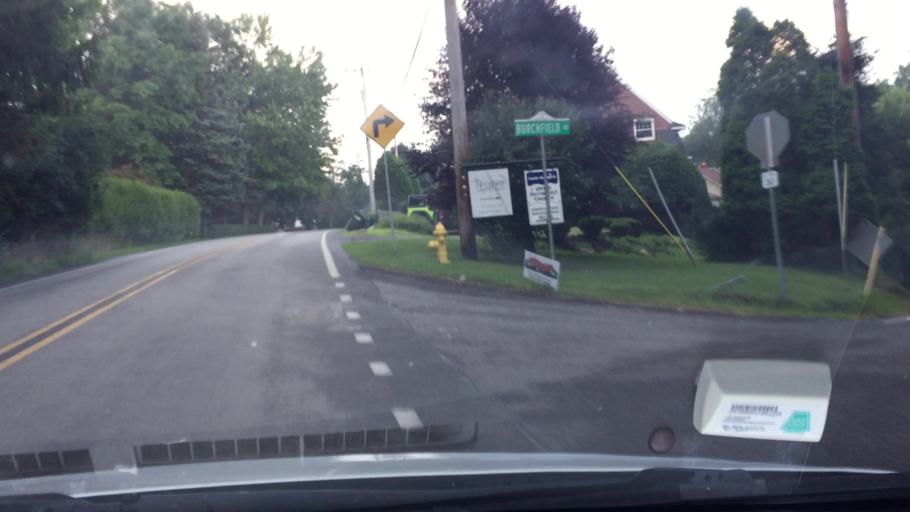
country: US
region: Pennsylvania
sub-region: Allegheny County
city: Allison Park
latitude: 40.5524
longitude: -79.9348
